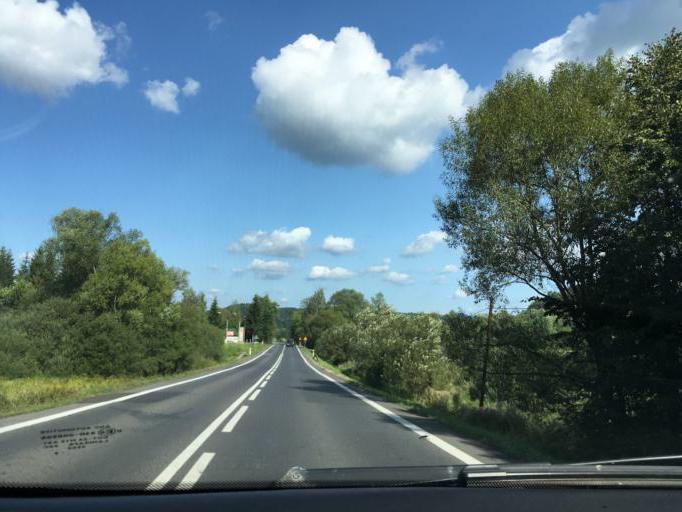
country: PL
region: Subcarpathian Voivodeship
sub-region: Powiat leski
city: Lesko
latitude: 49.4875
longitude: 22.3228
